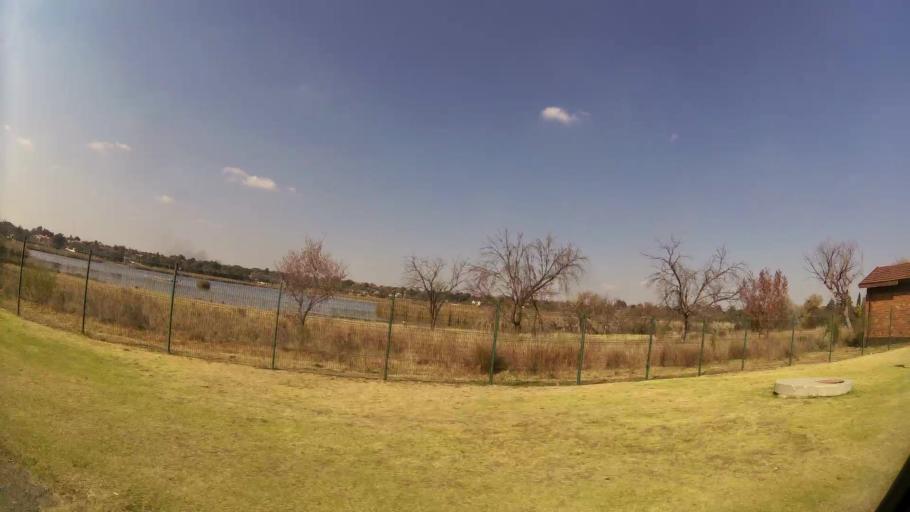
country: ZA
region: Gauteng
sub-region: Ekurhuleni Metropolitan Municipality
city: Benoni
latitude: -26.1912
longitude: 28.2905
